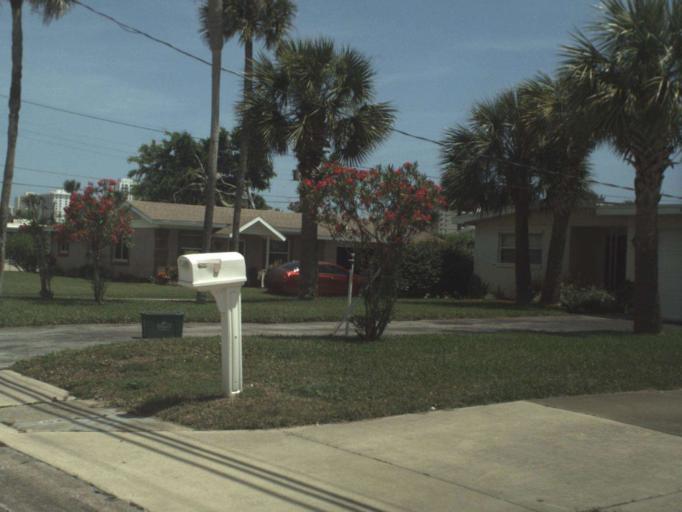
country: US
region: Florida
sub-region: Volusia County
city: Daytona Beach Shores
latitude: 29.1597
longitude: -80.9771
